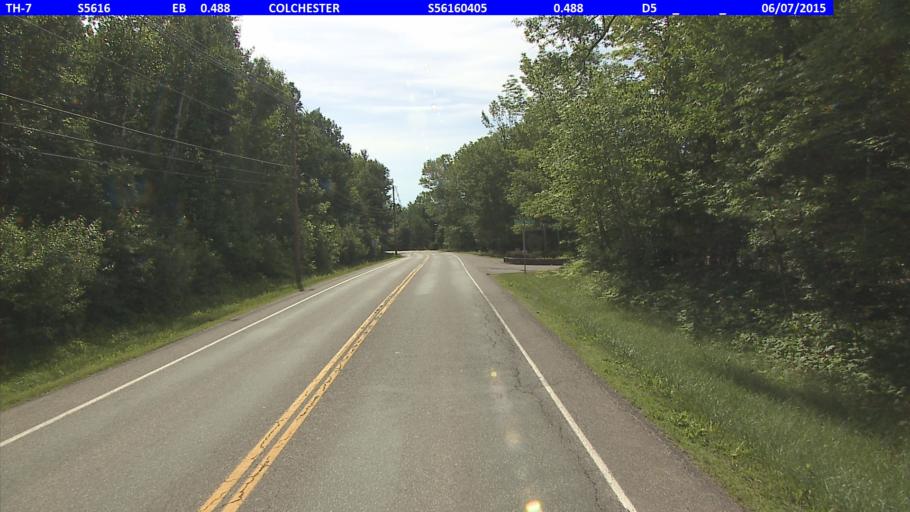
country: US
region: Vermont
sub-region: Chittenden County
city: Colchester
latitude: 44.5255
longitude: -73.1636
